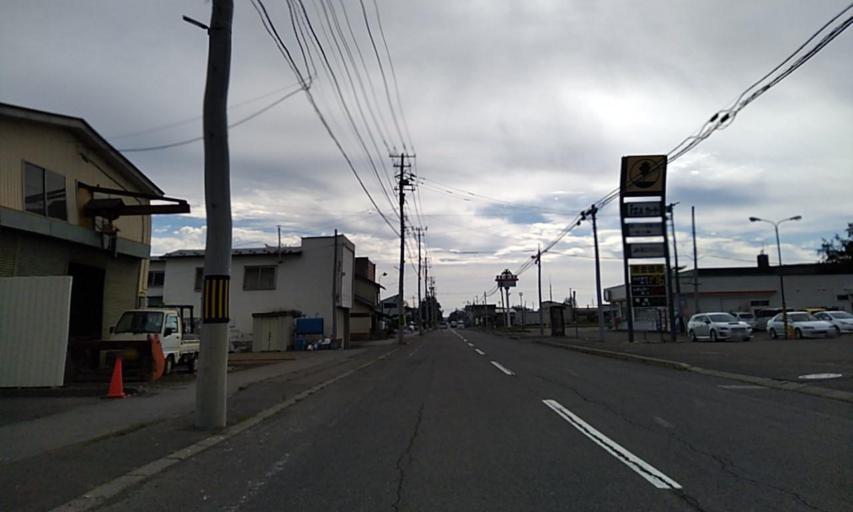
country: JP
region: Hokkaido
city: Obihiro
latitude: 42.8497
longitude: 143.1651
